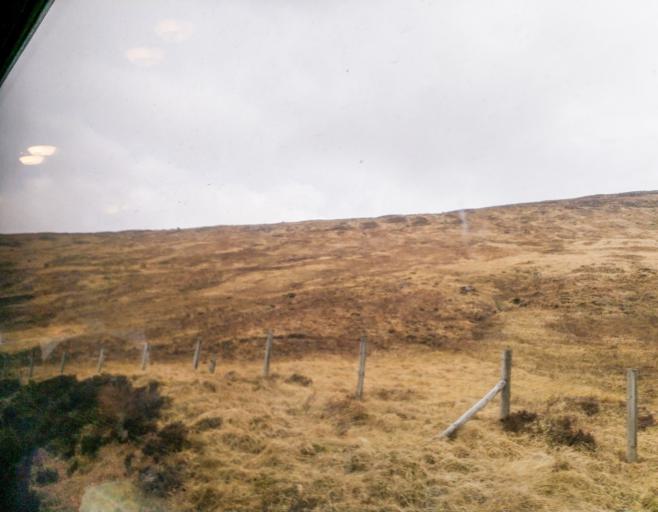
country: GB
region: Scotland
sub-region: Highland
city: Spean Bridge
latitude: 56.7753
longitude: -4.7159
